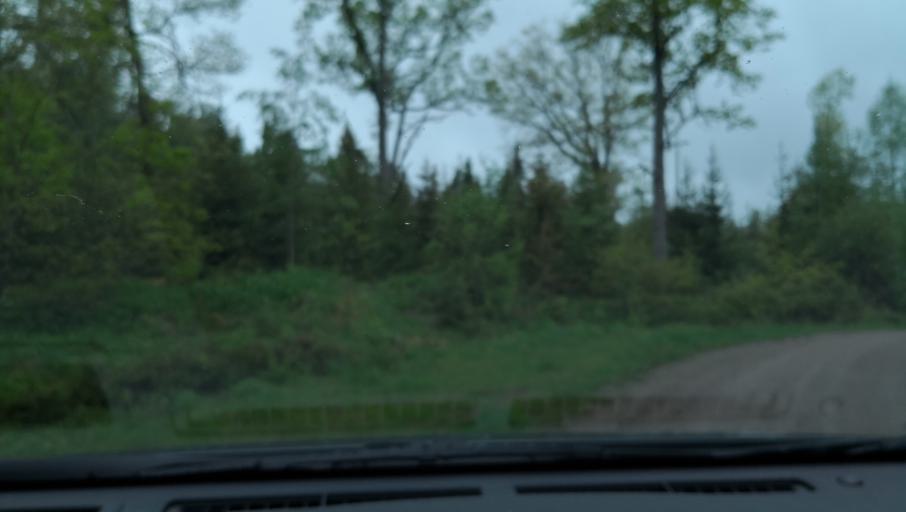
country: SE
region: Uppsala
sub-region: Enkopings Kommun
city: Orsundsbro
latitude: 59.9182
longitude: 17.3467
